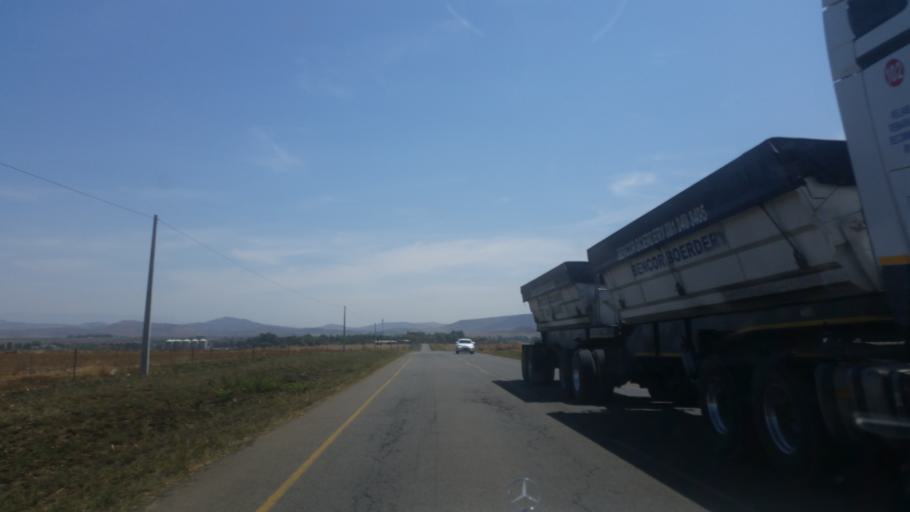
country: ZA
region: KwaZulu-Natal
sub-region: uThukela District Municipality
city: Bergville
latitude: -28.8194
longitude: 29.5611
